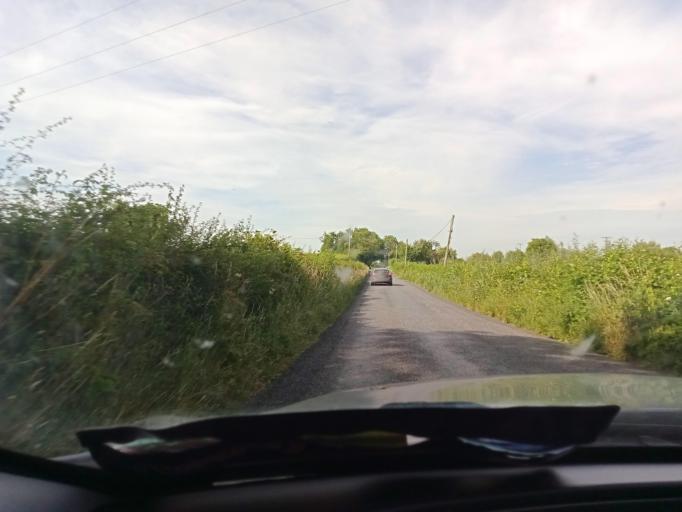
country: IE
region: Leinster
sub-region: Laois
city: Mountmellick
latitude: 53.1421
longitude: -7.3704
